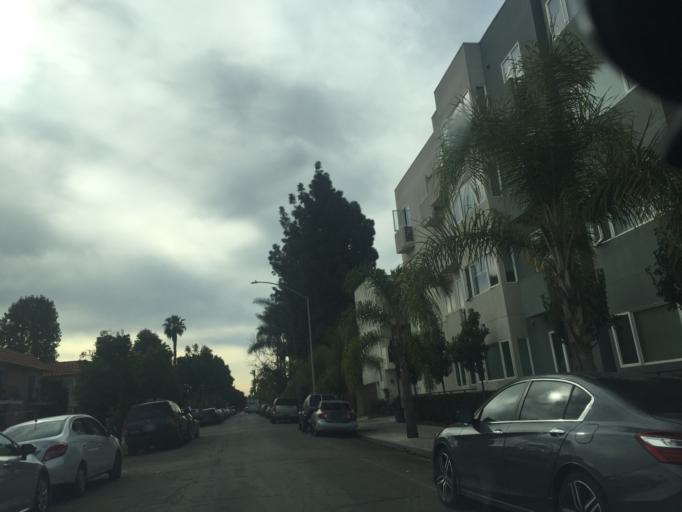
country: US
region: California
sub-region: San Diego County
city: Lemon Grove
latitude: 32.7550
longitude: -117.0998
